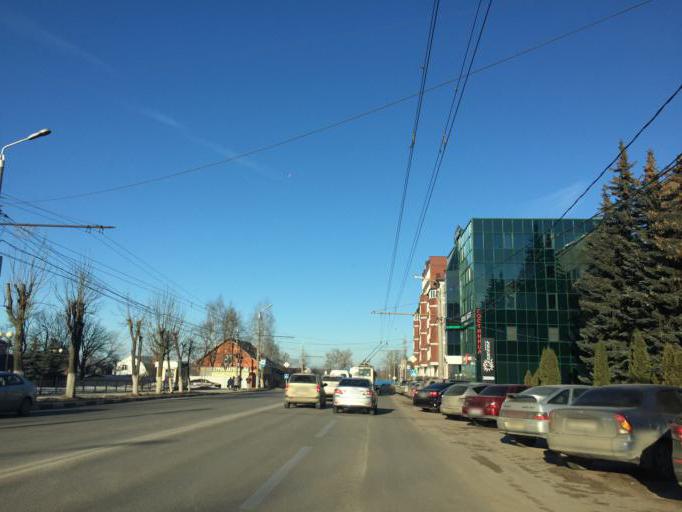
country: RU
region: Tula
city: Mendeleyevskiy
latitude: 54.1809
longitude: 37.5734
